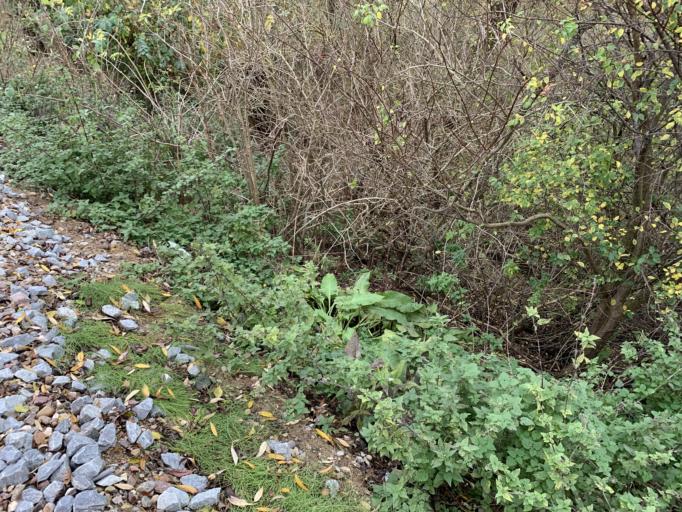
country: DK
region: Zealand
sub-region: Ringsted Kommune
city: Ringsted
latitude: 55.4010
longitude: 11.7421
